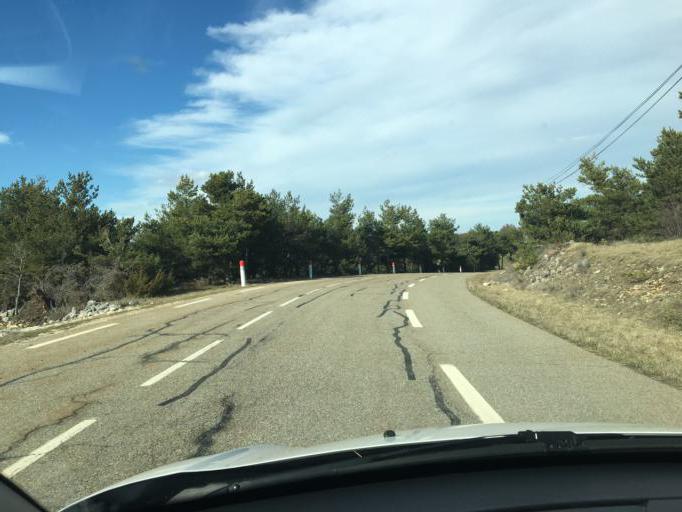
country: FR
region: Provence-Alpes-Cote d'Azur
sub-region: Departement du Vaucluse
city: Saint-Saturnin-les-Apt
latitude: 43.9953
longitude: 5.4783
